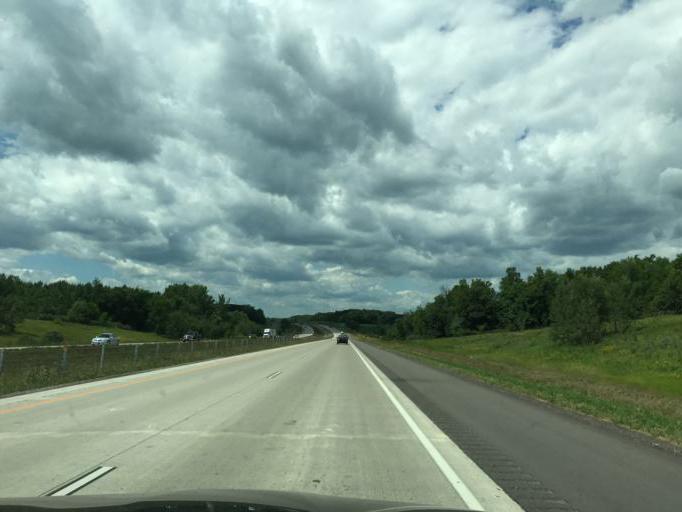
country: US
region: Minnesota
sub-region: Stearns County
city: Saint Joseph
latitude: 45.5390
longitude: -94.3180
